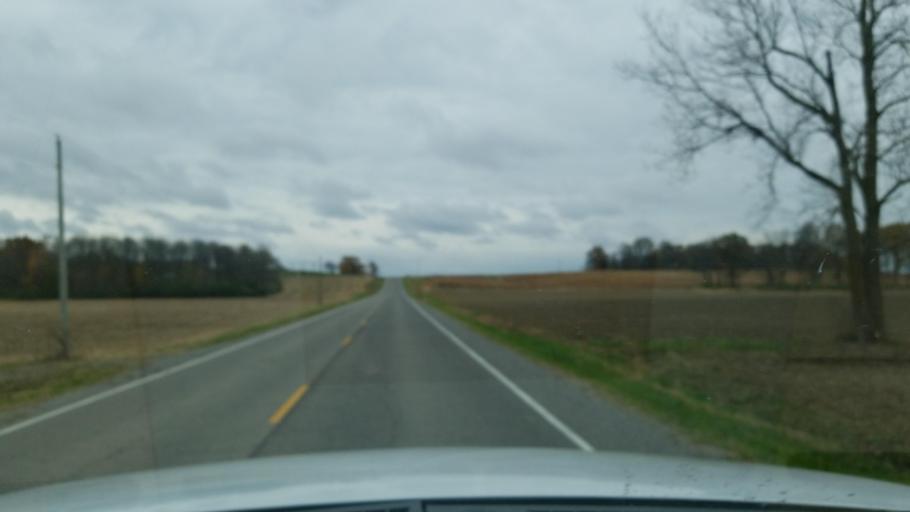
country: US
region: Illinois
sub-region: Saline County
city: Eldorado
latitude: 37.7579
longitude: -88.4383
